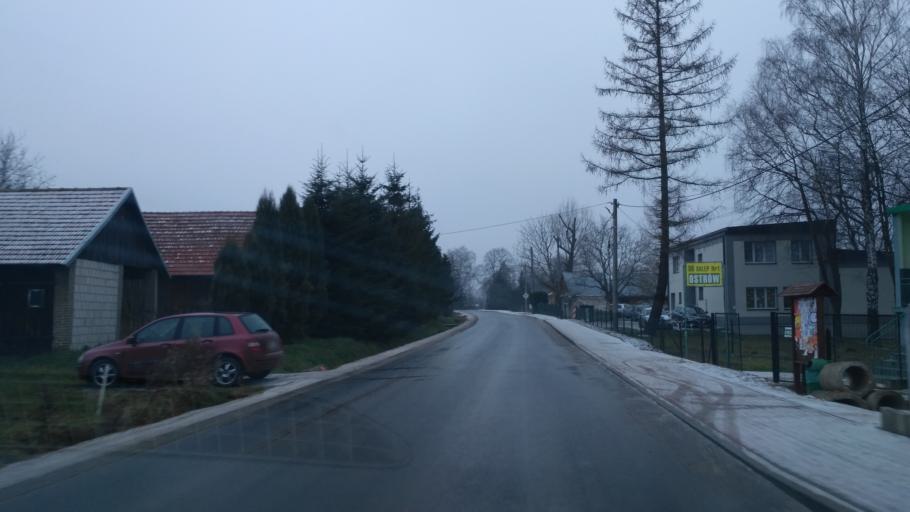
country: PL
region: Subcarpathian Voivodeship
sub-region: Powiat przeworski
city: Kanczuga
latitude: 50.0180
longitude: 22.3983
